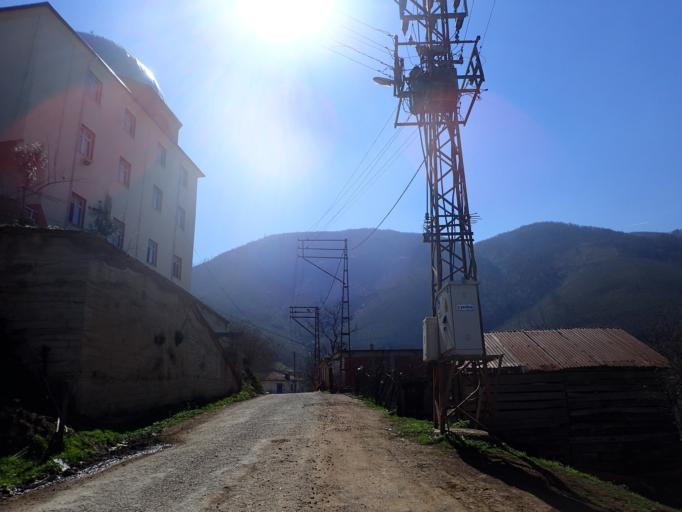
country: TR
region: Ordu
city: Catalpinar
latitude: 40.8657
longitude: 37.4933
